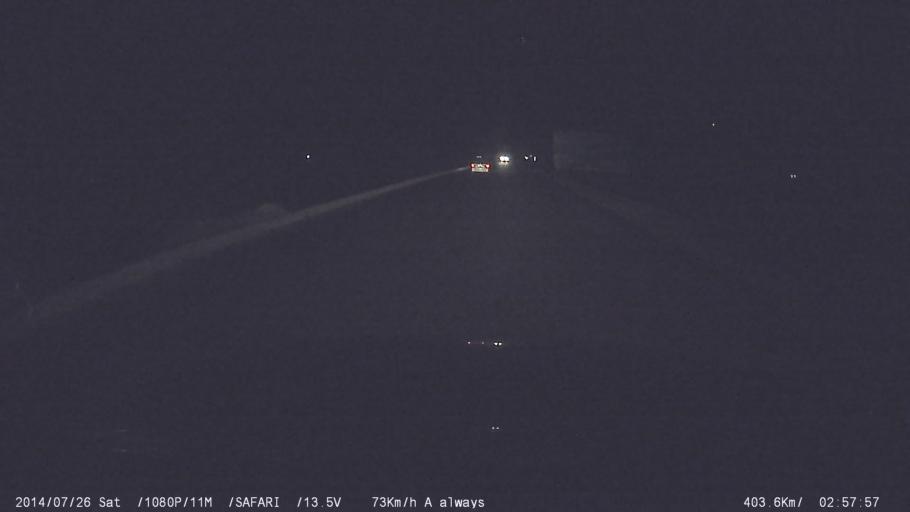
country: IN
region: Kerala
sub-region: Palakkad district
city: Palakkad
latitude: 10.7379
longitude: 76.6249
